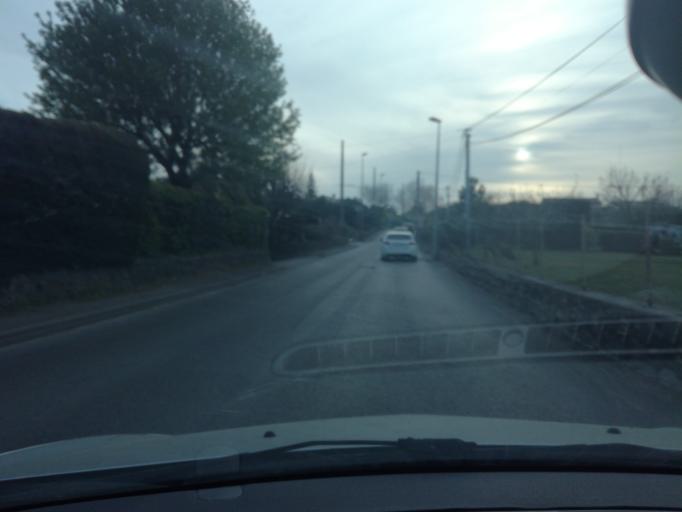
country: FR
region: Provence-Alpes-Cote d'Azur
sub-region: Departement des Alpes-Maritimes
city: Grasse
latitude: 43.6373
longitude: 6.9295
